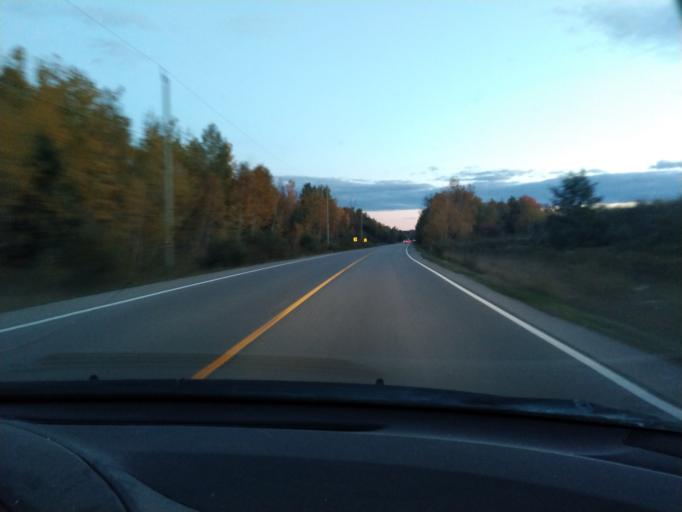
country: CA
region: Ontario
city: Bradford West Gwillimbury
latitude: 44.1891
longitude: -79.6619
